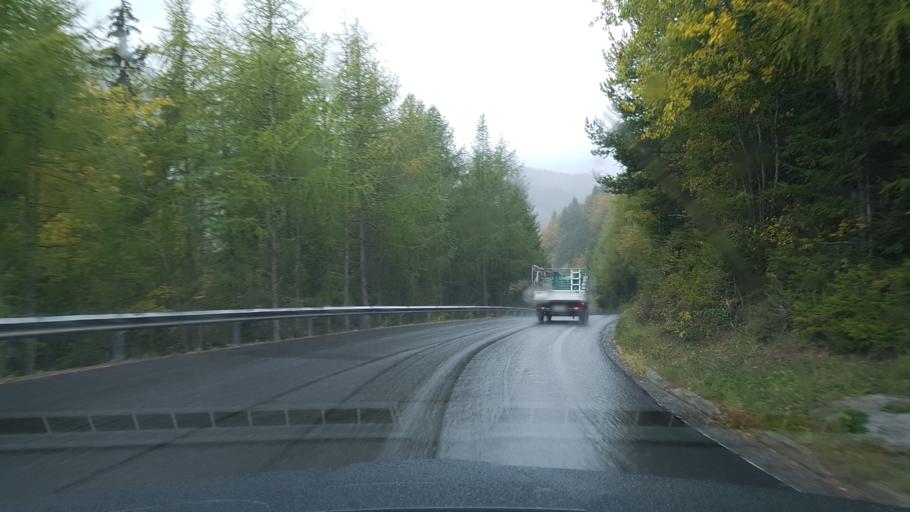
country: AT
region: Styria
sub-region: Politischer Bezirk Voitsberg
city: Salla
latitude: 47.1062
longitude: 14.9576
